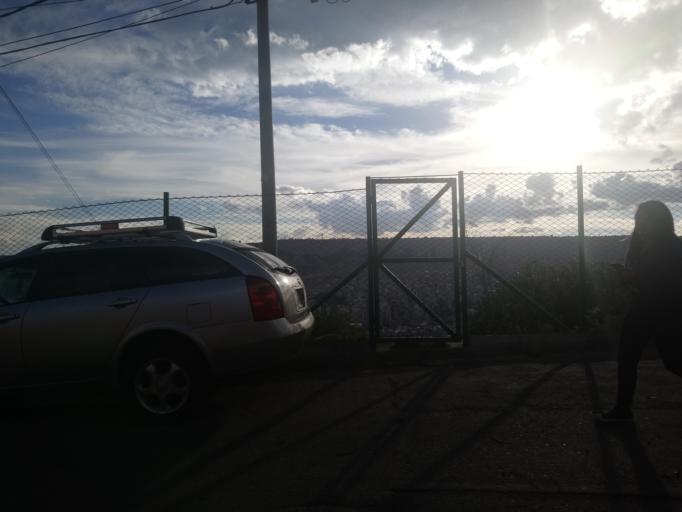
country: BO
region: La Paz
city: La Paz
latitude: -16.5015
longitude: -68.1057
